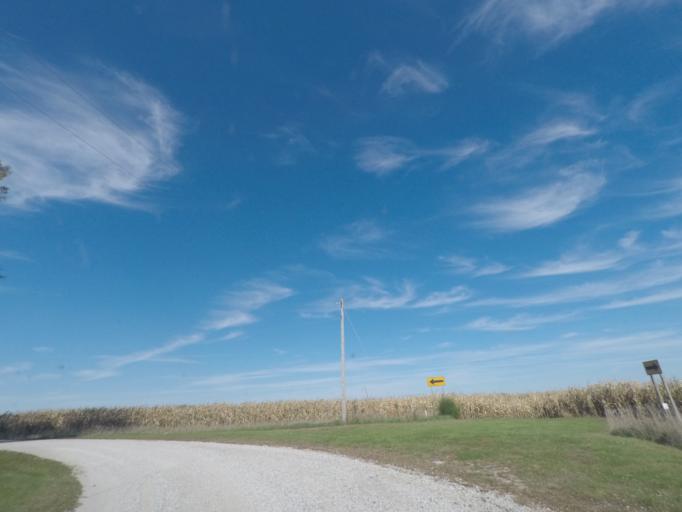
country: US
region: Iowa
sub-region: Story County
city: Nevada
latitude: 42.0119
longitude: -93.3476
